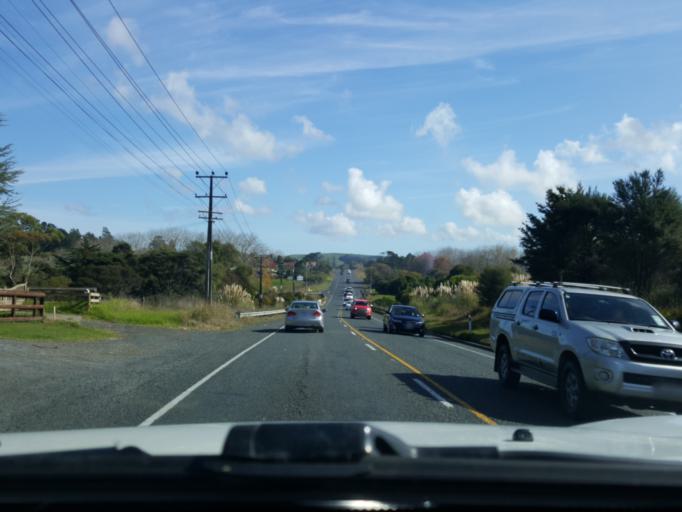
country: NZ
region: Auckland
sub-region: Auckland
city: Muriwai Beach
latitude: -36.7667
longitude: 174.5151
